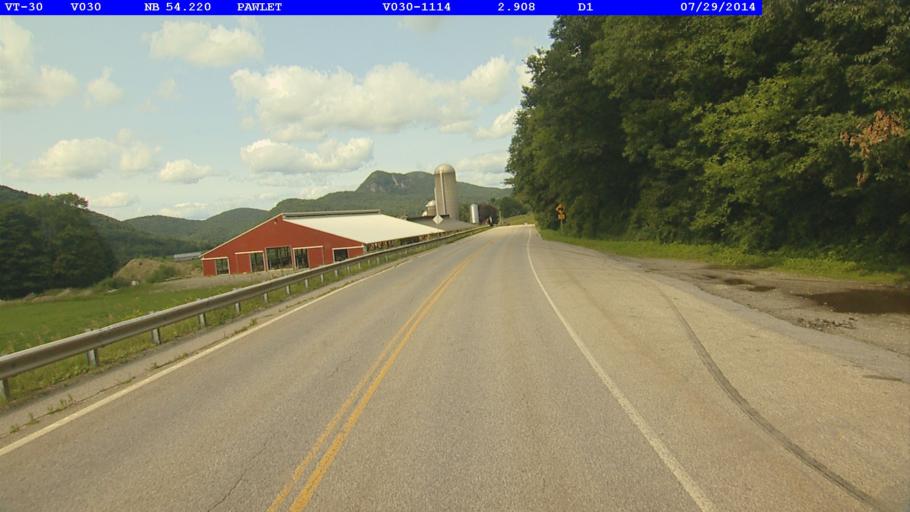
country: US
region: New York
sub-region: Washington County
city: Granville
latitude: 43.3495
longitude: -73.1826
